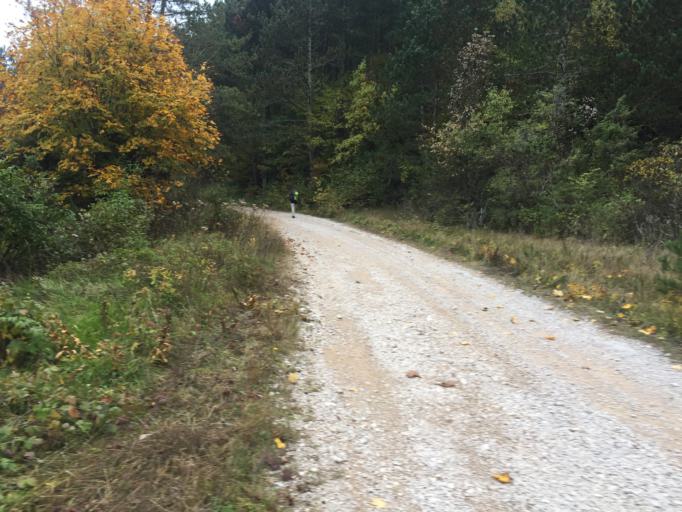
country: HR
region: Istarska
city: Buzet
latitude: 45.4101
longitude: 14.1312
